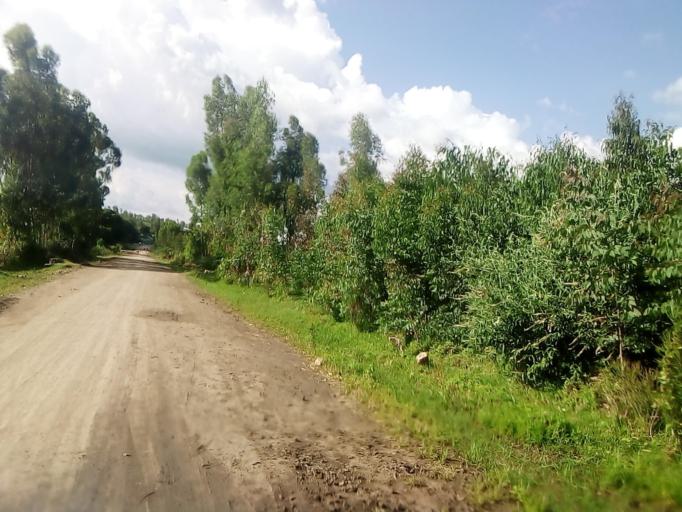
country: ET
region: Southern Nations, Nationalities, and People's Region
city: K'olito
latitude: 7.6623
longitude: 38.0474
